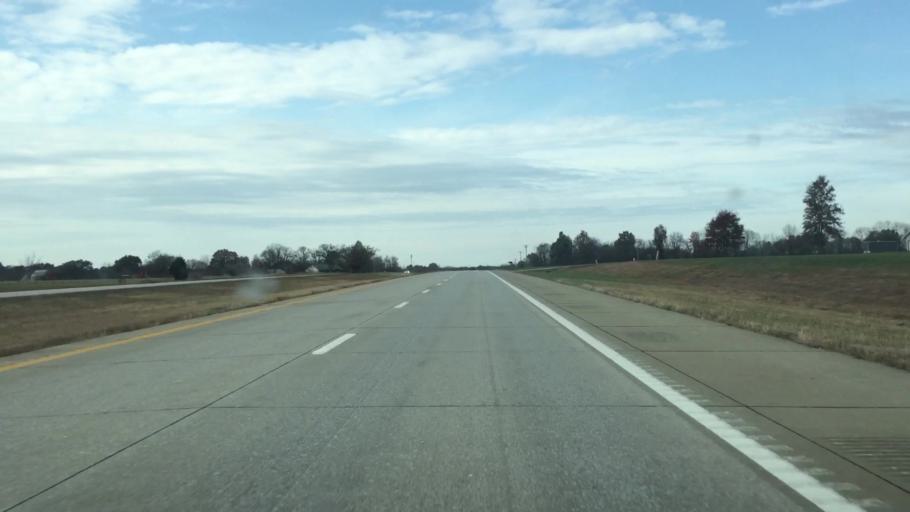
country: US
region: Missouri
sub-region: Henry County
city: Clinton
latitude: 38.4547
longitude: -93.9633
